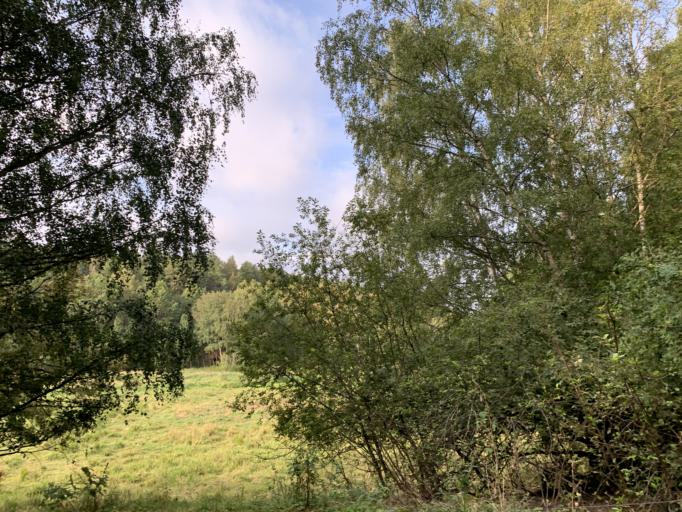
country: SE
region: Stockholm
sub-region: Solna Kommun
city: Rasunda
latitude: 59.3932
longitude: 17.9829
